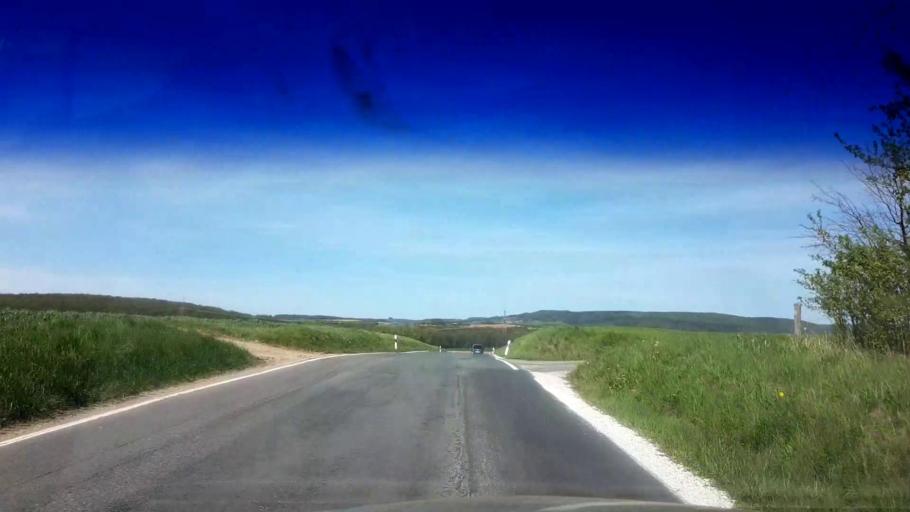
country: DE
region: Bavaria
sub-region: Upper Franconia
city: Schesslitz
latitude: 49.9568
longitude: 11.0154
